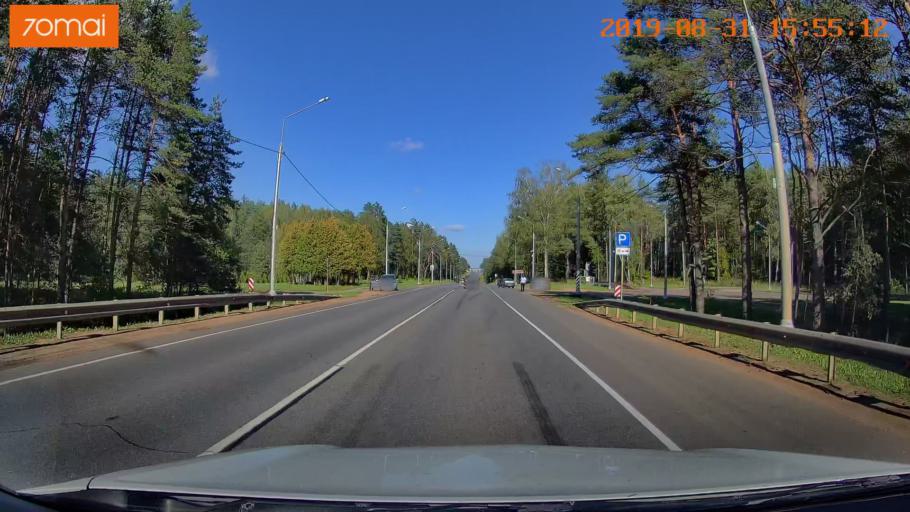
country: RU
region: Kaluga
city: Yukhnov
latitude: 54.7237
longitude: 35.1654
